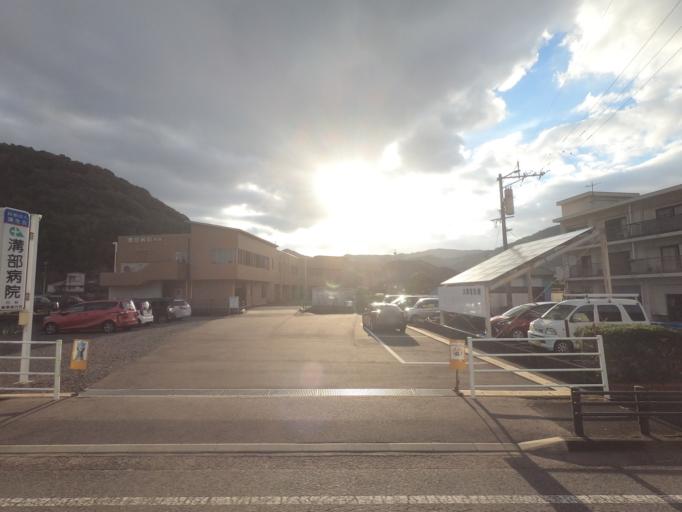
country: JP
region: Kumamoto
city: Minamata
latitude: 32.2691
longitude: 130.5041
